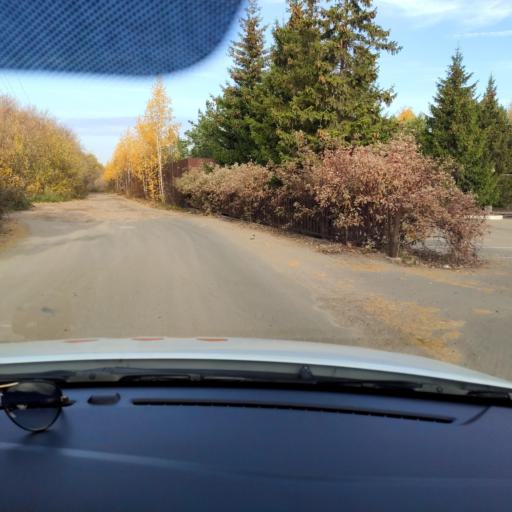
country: RU
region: Tatarstan
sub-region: Gorod Kazan'
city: Kazan
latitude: 55.8075
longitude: 49.0623
